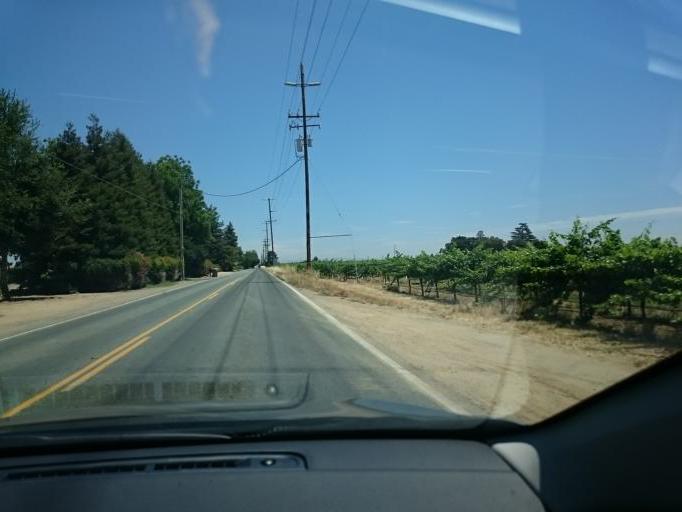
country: US
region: California
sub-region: San Joaquin County
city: Collierville
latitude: 38.1892
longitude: -121.2940
